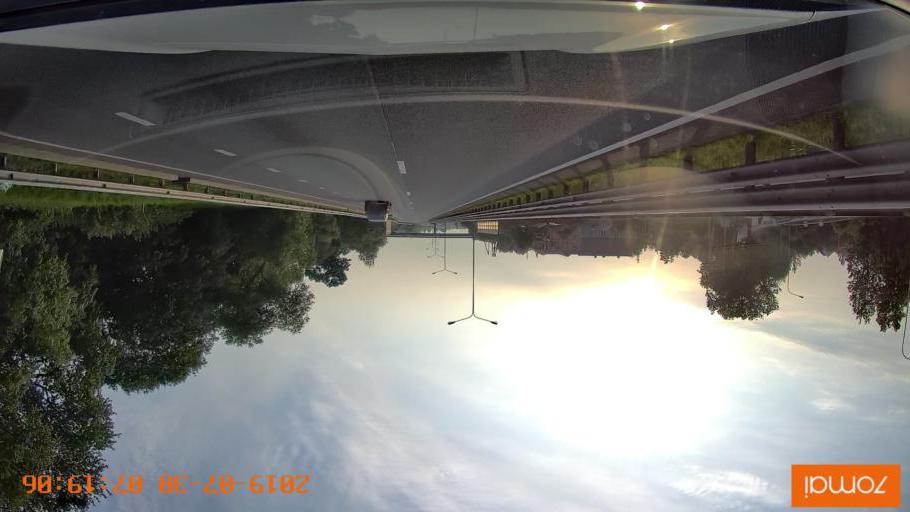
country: RU
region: Kaliningrad
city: Bol'shoe Isakovo
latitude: 54.7017
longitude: 20.6656
